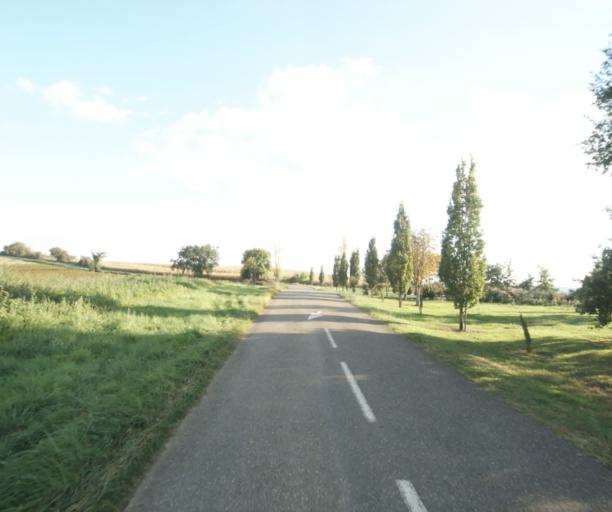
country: FR
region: Midi-Pyrenees
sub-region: Departement du Gers
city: Eauze
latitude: 43.7437
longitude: 0.1363
